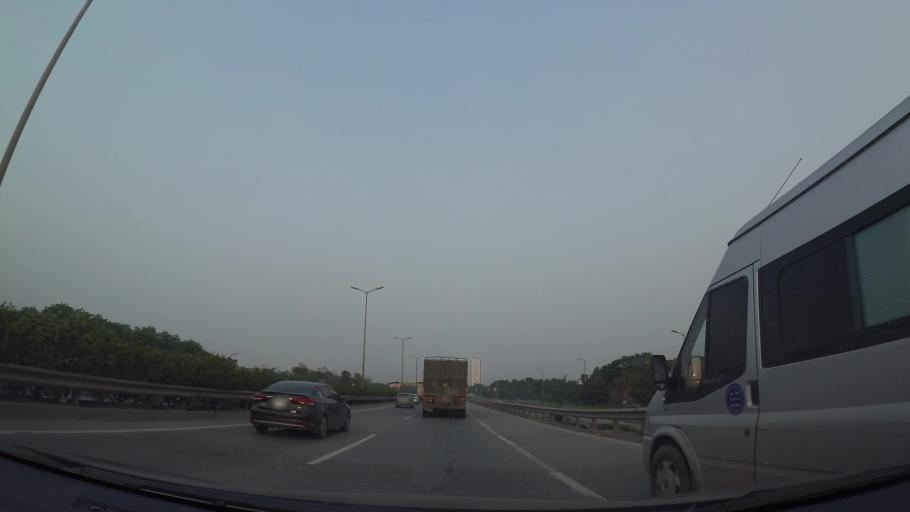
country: VN
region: Ha Noi
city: Van Dien
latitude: 20.9652
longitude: 105.8537
